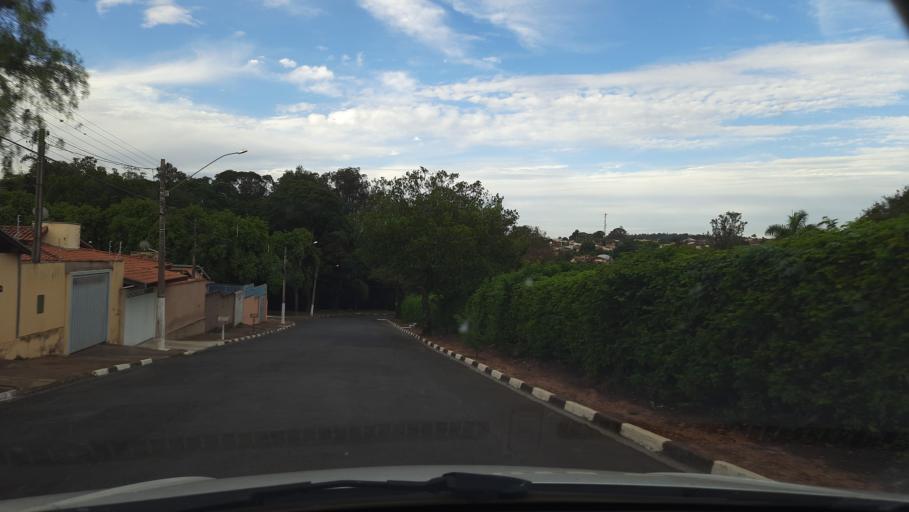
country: BR
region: Sao Paulo
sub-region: Casa Branca
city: Casa Branca
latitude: -21.7836
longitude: -47.0890
